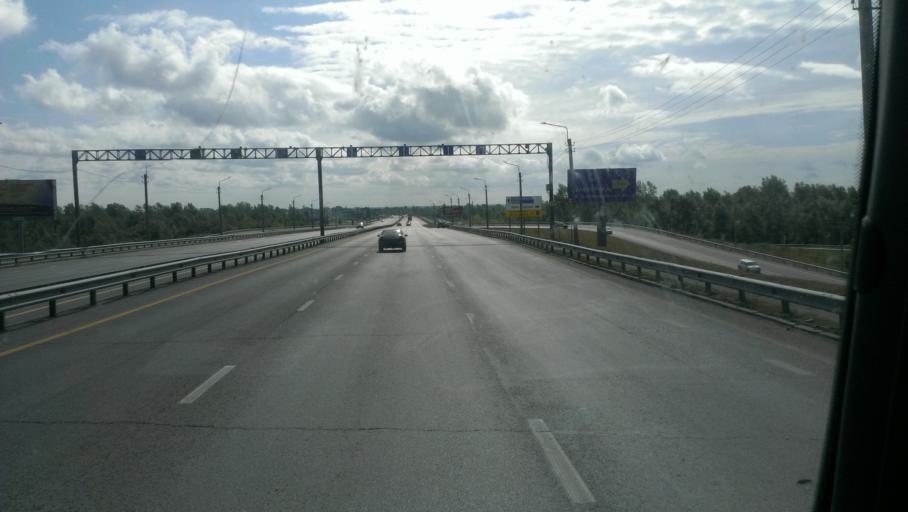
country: RU
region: Altai Krai
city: Zaton
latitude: 53.3206
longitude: 83.8116
